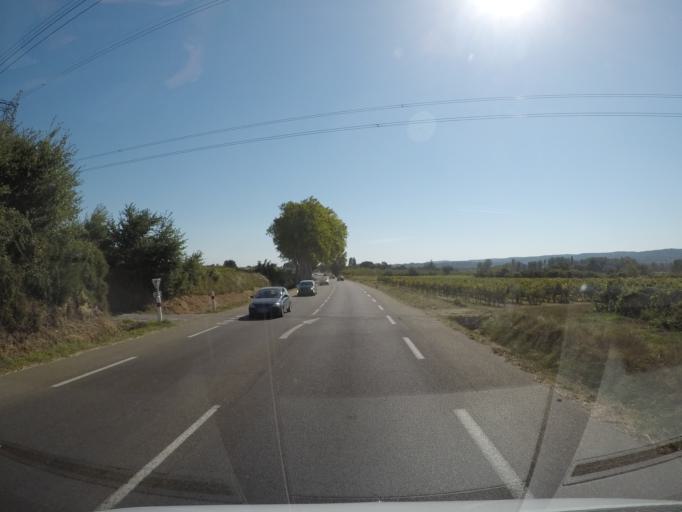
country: FR
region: Languedoc-Roussillon
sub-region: Departement du Gard
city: Uzes
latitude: 43.9829
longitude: 4.4649
